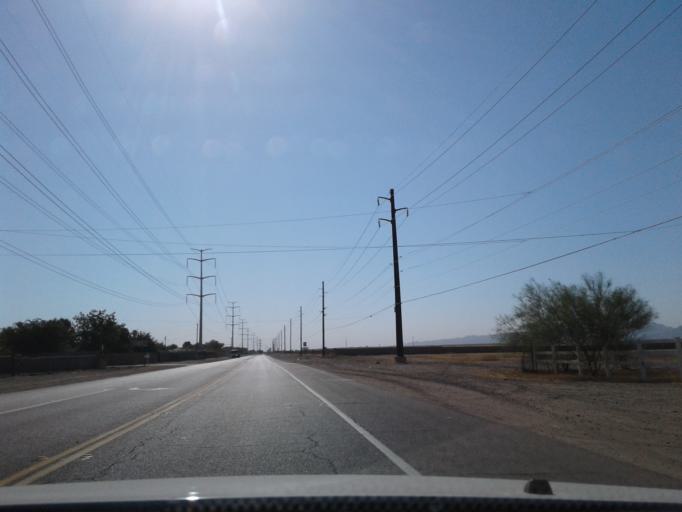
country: US
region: Arizona
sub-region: Maricopa County
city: Laveen
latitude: 33.4084
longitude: -112.2037
